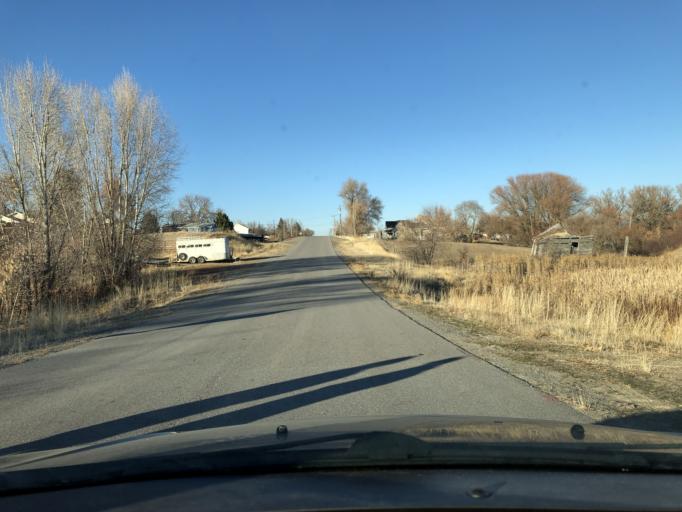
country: US
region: Utah
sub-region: Cache County
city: Wellsville
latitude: 41.6309
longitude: -111.9319
